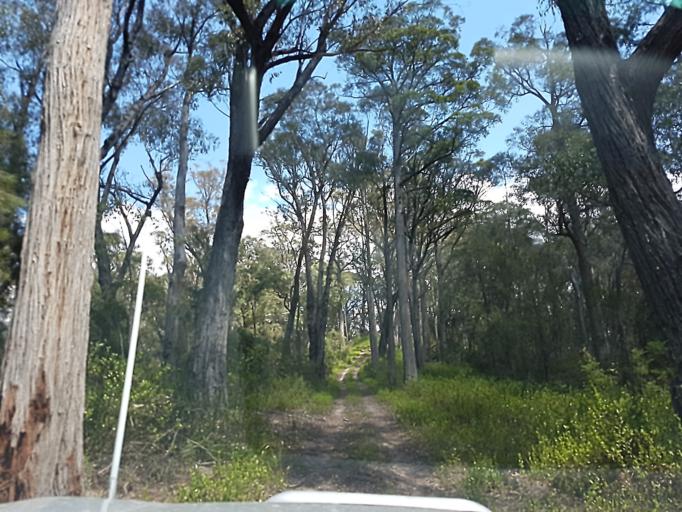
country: AU
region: Victoria
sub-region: East Gippsland
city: Lakes Entrance
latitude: -37.3114
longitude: 148.3526
